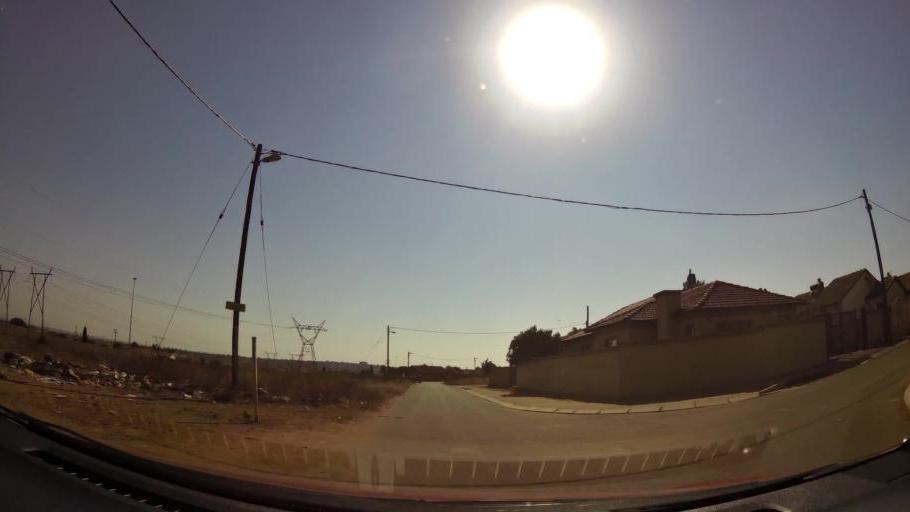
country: ZA
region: Gauteng
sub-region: City of Tshwane Metropolitan Municipality
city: Mabopane
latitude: -25.5537
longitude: 28.0796
